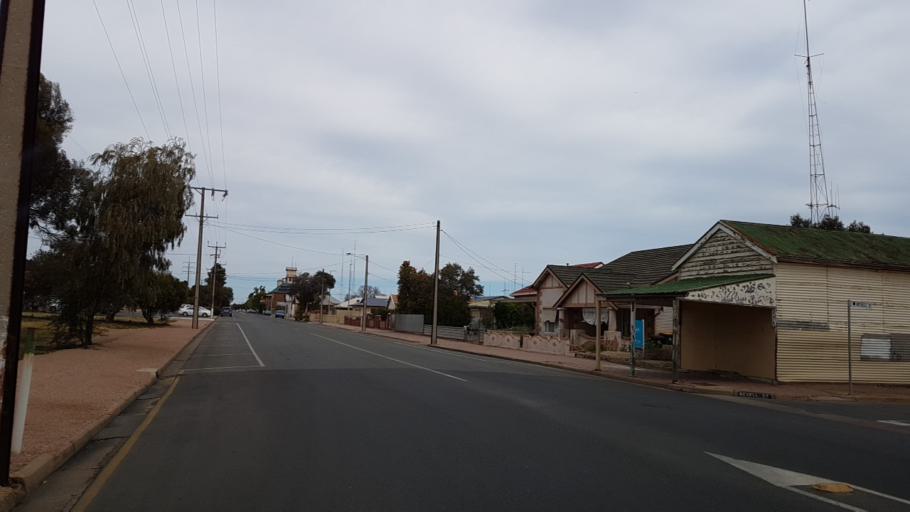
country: AU
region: South Australia
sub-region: Port Pirie City and Dists
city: Port Pirie
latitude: -33.1755
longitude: 138.0040
